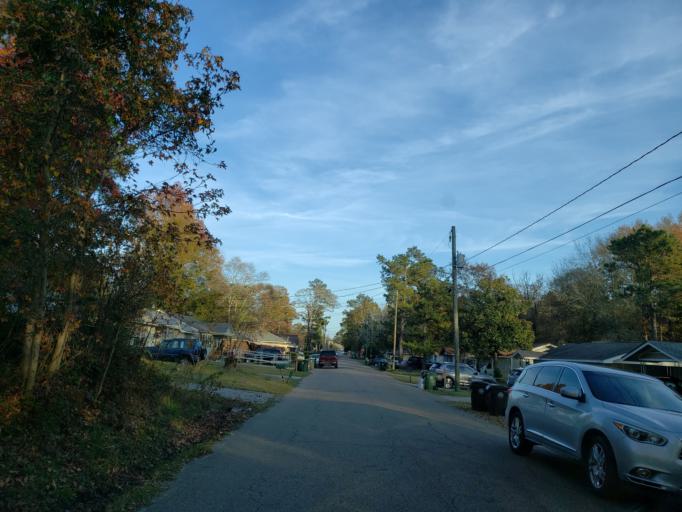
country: US
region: Mississippi
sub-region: Forrest County
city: Hattiesburg
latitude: 31.3284
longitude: -89.3161
